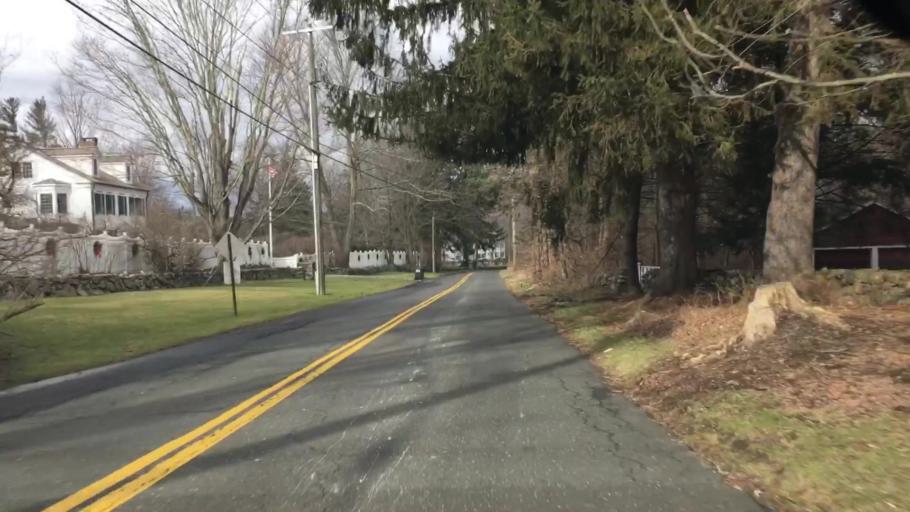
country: US
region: New York
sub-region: Putnam County
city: Peach Lake
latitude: 41.3622
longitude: -73.5250
